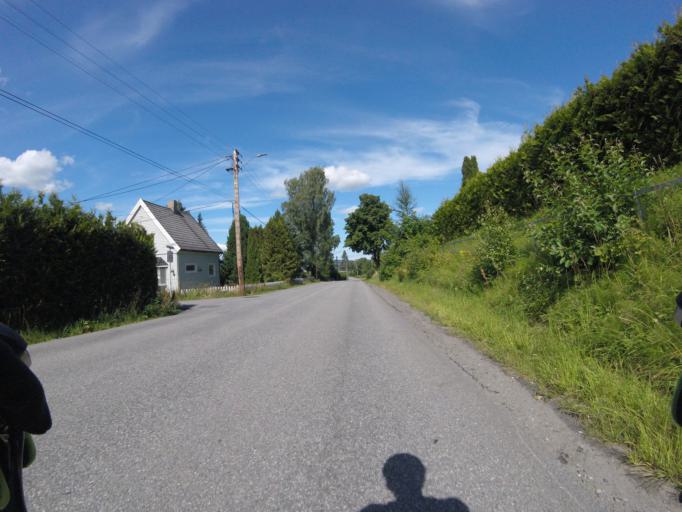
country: NO
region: Akershus
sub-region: Skedsmo
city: Lillestrom
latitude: 59.9475
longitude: 11.0207
